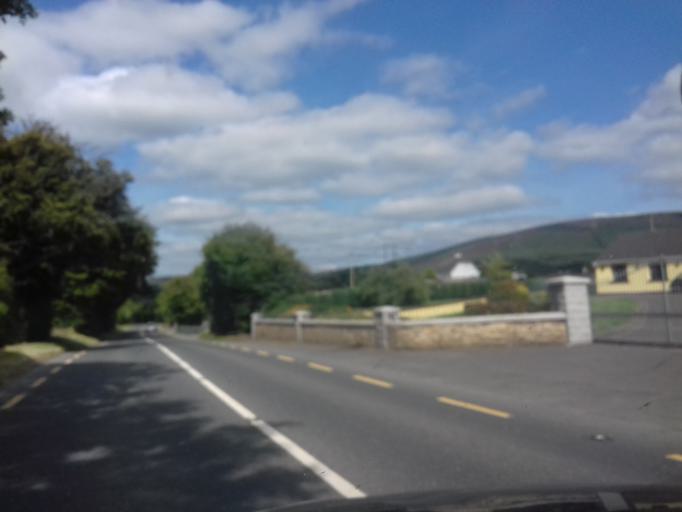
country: IE
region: Leinster
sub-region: Wicklow
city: Valleymount
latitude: 53.0487
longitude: -6.6321
